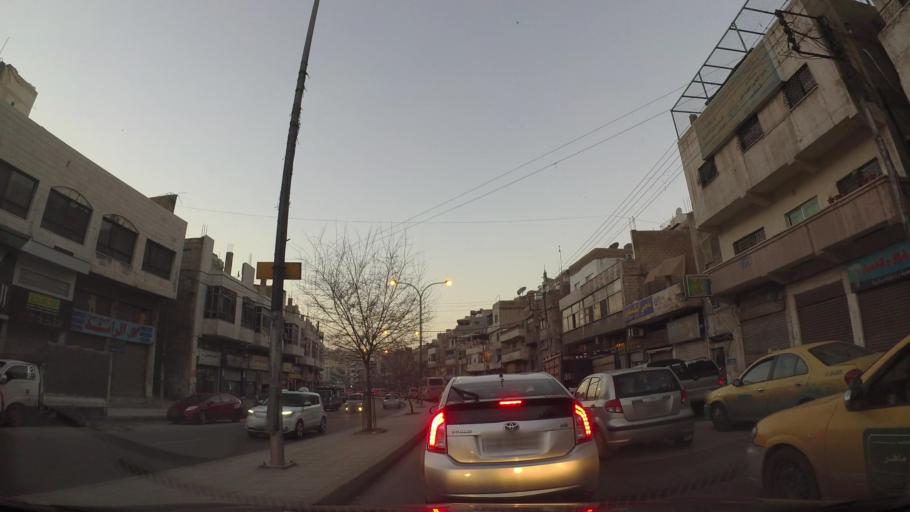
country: JO
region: Amman
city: Amman
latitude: 31.9382
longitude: 35.9238
